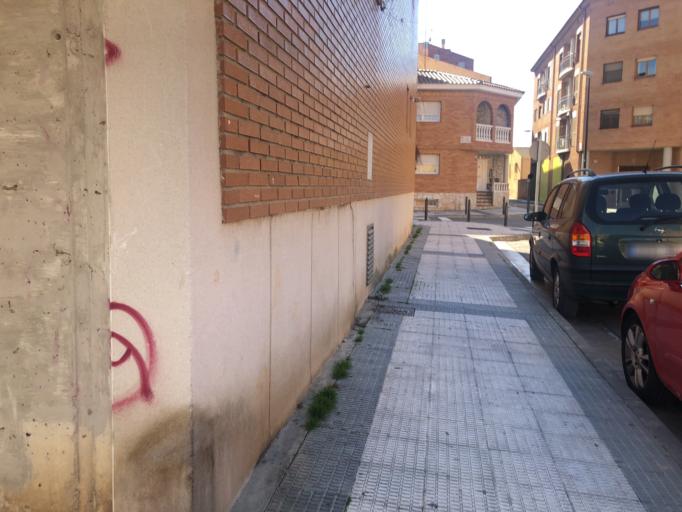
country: ES
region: Aragon
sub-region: Provincia de Zaragoza
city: Zaragoza
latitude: 41.6676
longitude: -0.8267
